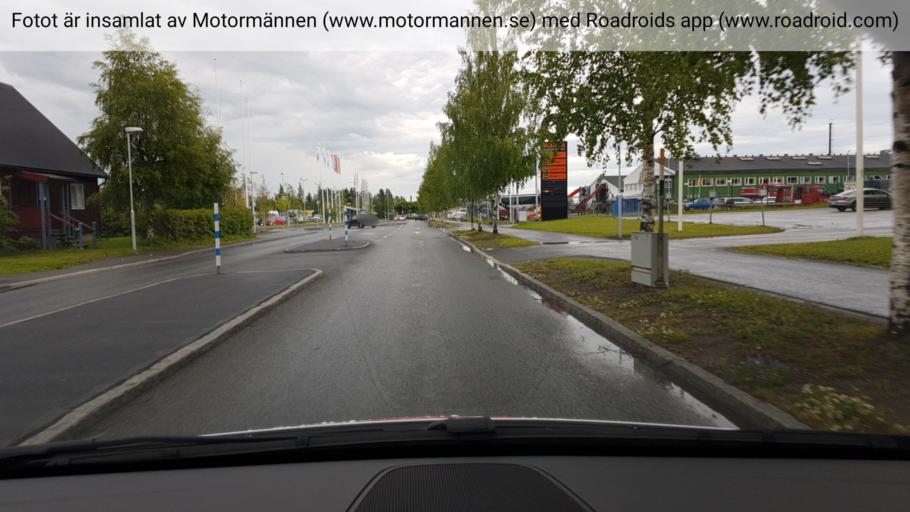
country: SE
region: Jaemtland
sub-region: OEstersunds Kommun
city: Ostersund
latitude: 63.1724
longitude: 14.6895
